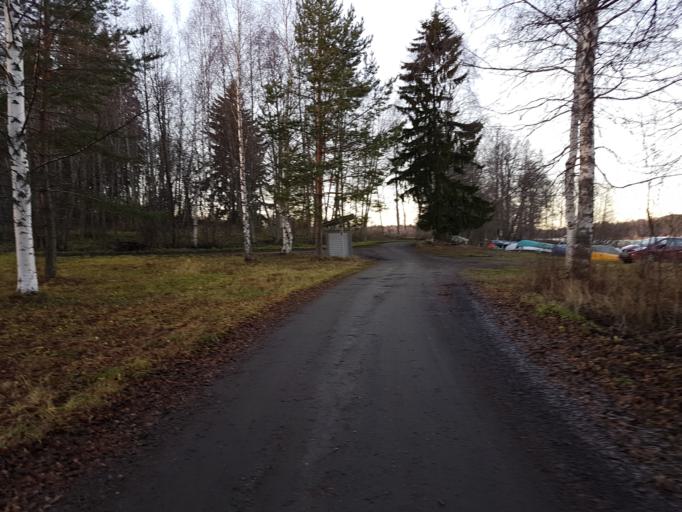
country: FI
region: Northern Savo
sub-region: Kuopio
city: Kuopio
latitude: 62.9285
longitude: 27.6276
